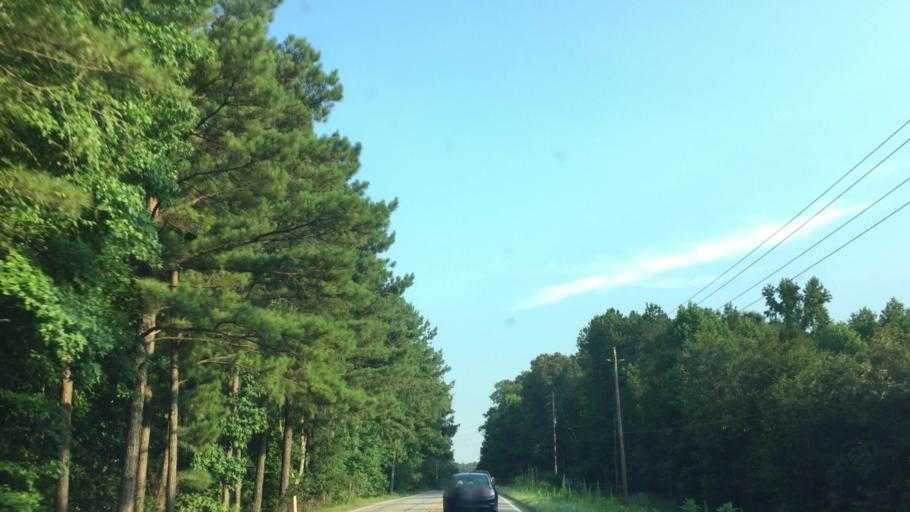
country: US
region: Georgia
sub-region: DeKalb County
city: Pine Mountain
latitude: 33.6366
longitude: -84.1842
